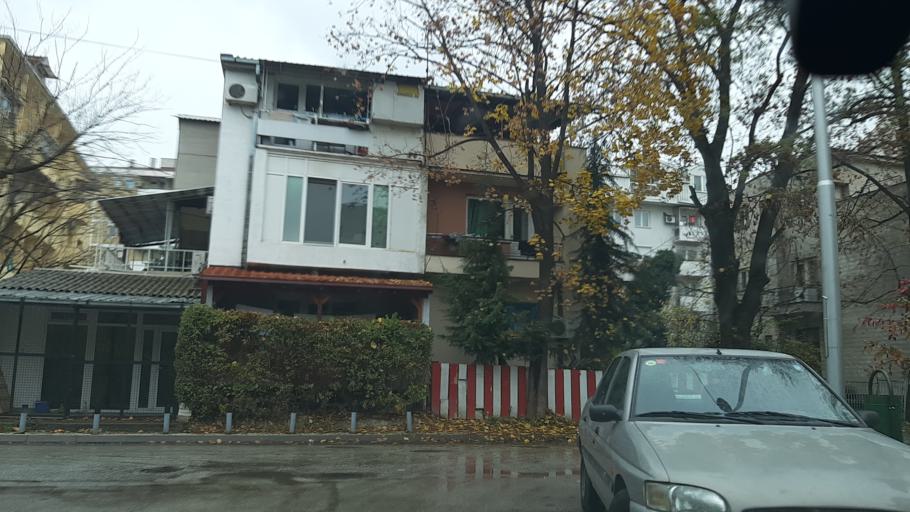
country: MK
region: Karpos
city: Skopje
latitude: 41.9884
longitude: 21.4466
